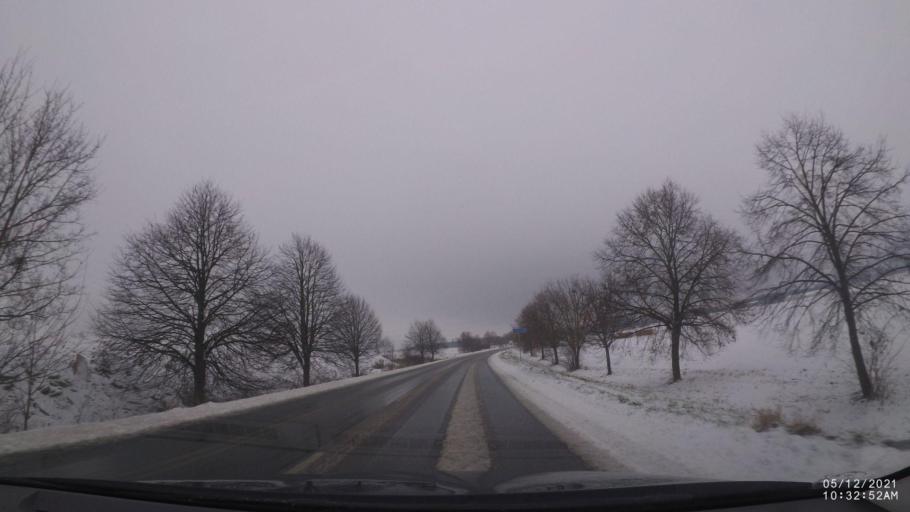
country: CZ
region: Kralovehradecky
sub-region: Okres Rychnov nad Kneznou
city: Rychnov nad Kneznou
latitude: 50.1628
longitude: 16.2912
